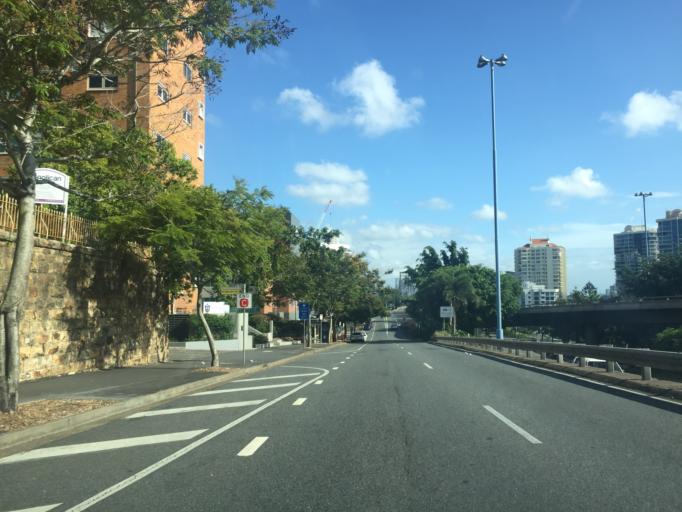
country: AU
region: Queensland
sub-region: Brisbane
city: Brisbane
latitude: -27.4746
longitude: 153.0356
